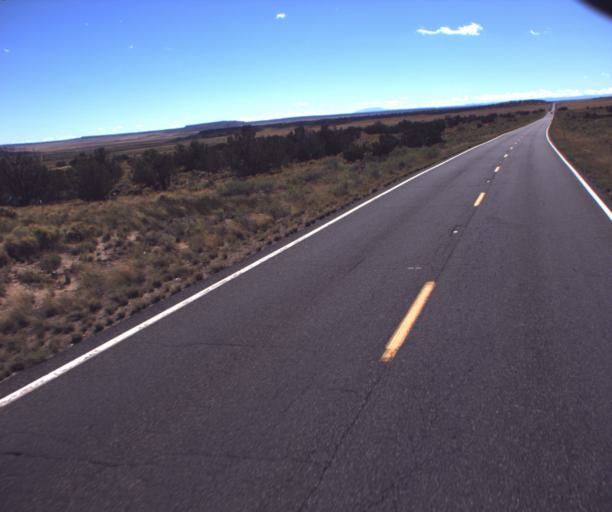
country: US
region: Arizona
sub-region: Apache County
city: Saint Johns
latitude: 34.7806
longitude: -109.2386
